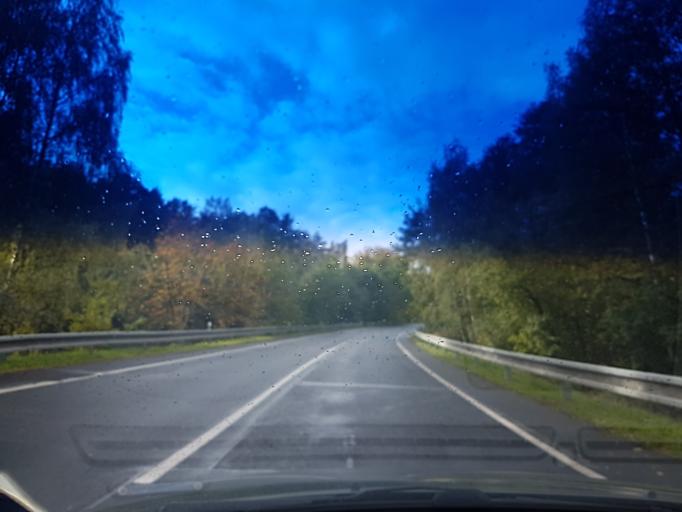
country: CZ
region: Karlovarsky
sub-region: Okres Cheb
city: Cheb
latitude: 50.0713
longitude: 12.3537
